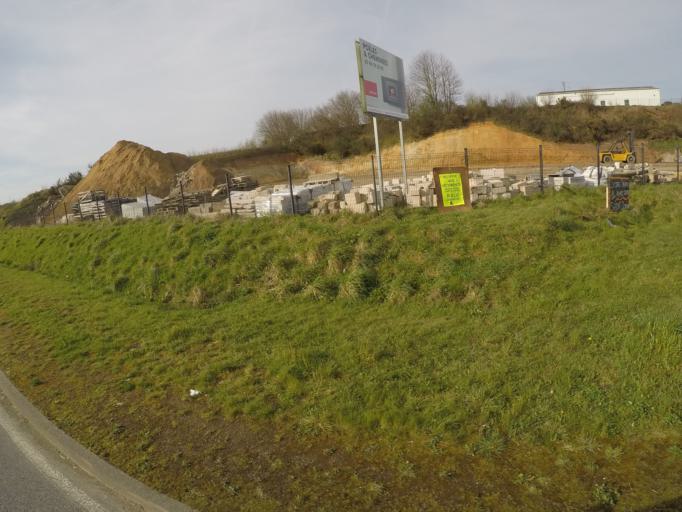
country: FR
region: Brittany
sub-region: Departement des Cotes-d'Armor
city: Plouagat
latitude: 48.5288
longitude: -2.9680
